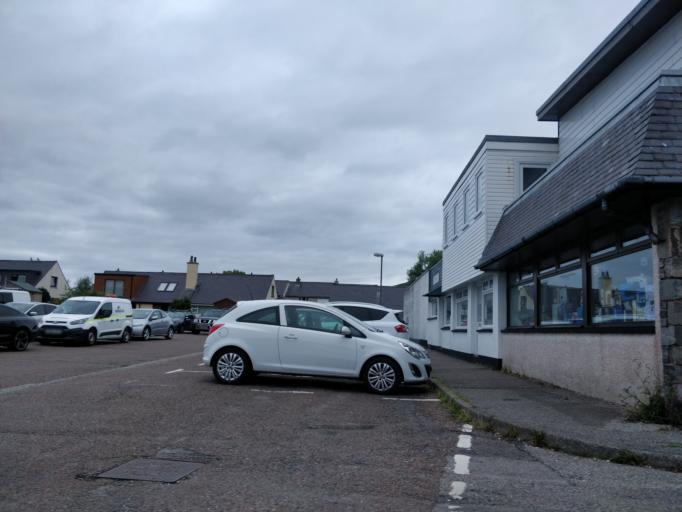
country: GB
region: Scotland
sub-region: Highland
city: Ullapool
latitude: 57.8974
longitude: -5.1642
